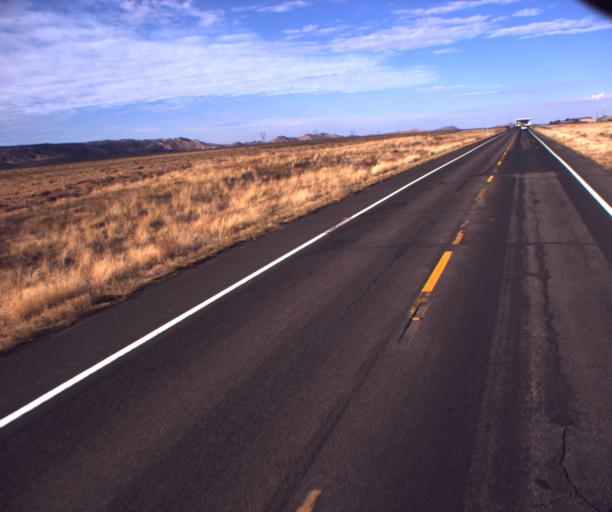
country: US
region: Arizona
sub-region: Apache County
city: Lukachukai
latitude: 36.9604
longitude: -109.3674
